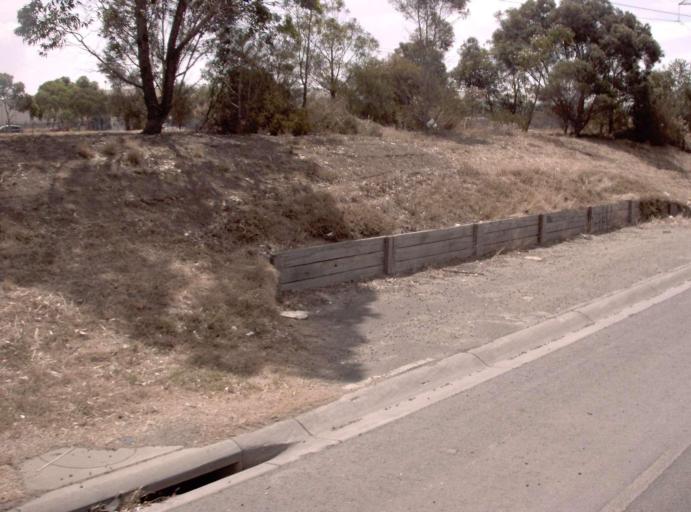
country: AU
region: Victoria
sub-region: Brimbank
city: Sunshine West
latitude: -37.8086
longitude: 144.8074
